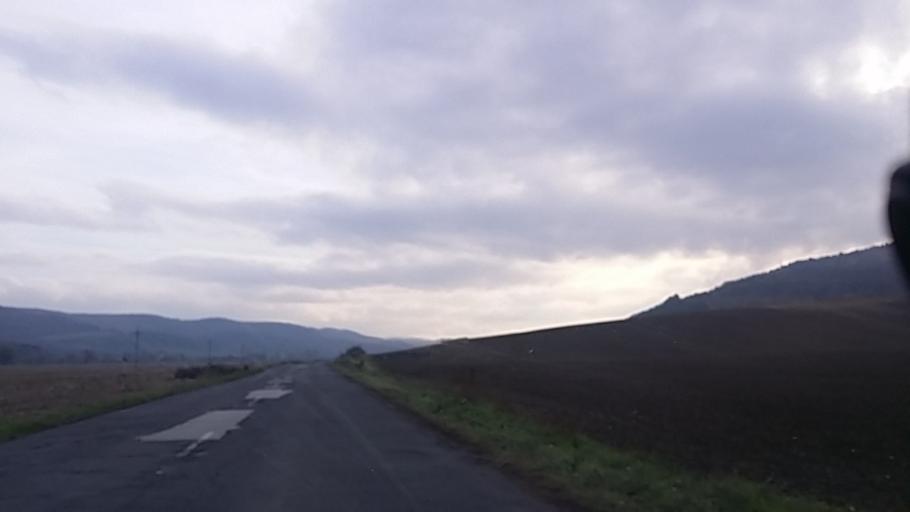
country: HU
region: Borsod-Abauj-Zemplen
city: Sajokaza
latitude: 48.2647
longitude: 20.5414
